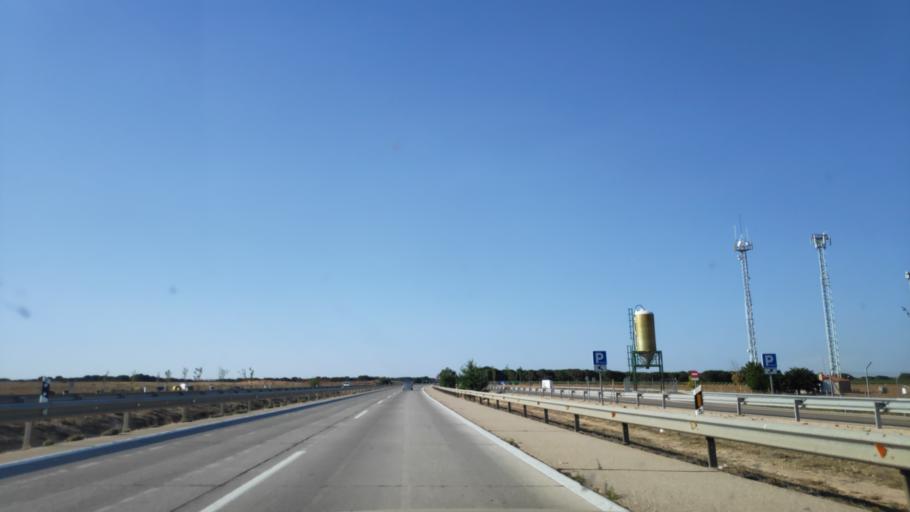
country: ES
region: Castille-La Mancha
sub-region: Provincia de Cuenca
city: Pozoamargo
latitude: 39.3212
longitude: -2.2032
